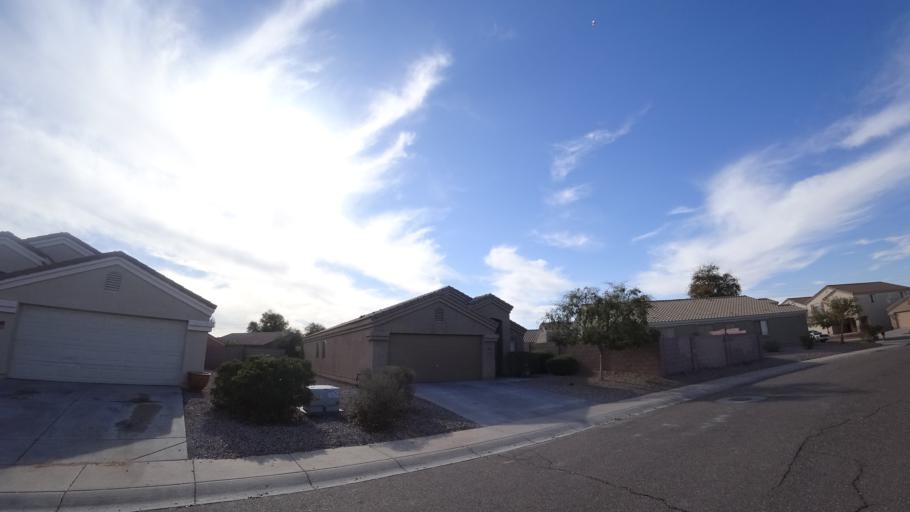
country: US
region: Arizona
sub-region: Maricopa County
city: Tolleson
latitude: 33.4258
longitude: -112.2880
